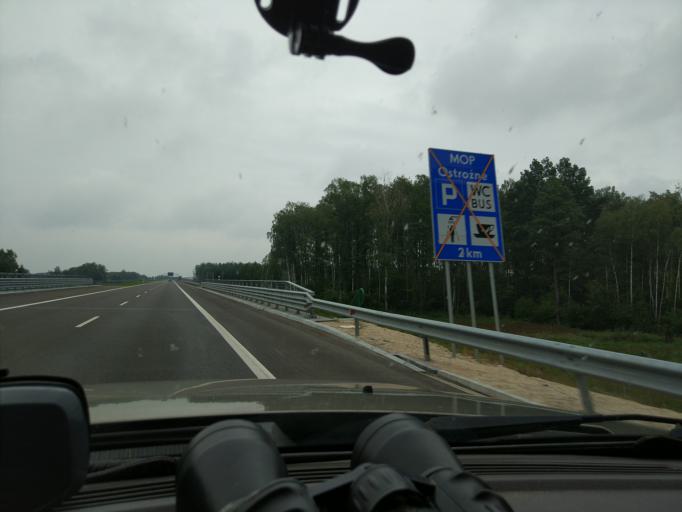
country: PL
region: Podlasie
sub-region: Powiat zambrowski
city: Szumowo
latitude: 52.9344
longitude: 22.1405
